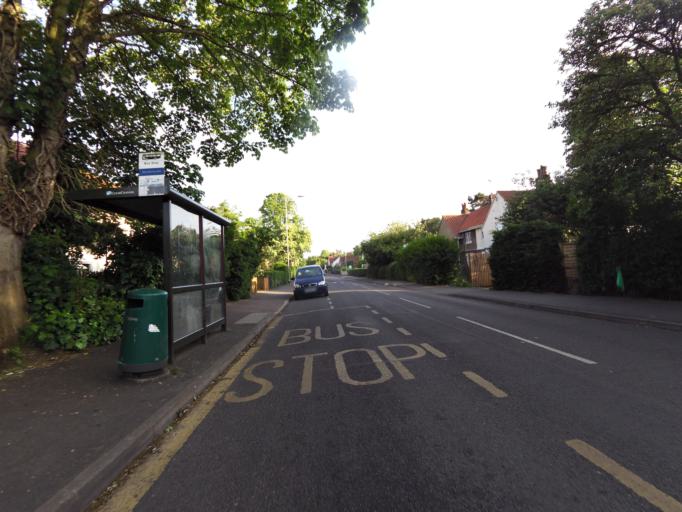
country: GB
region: England
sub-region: Norfolk
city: Norwich
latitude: 52.6480
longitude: 1.2910
